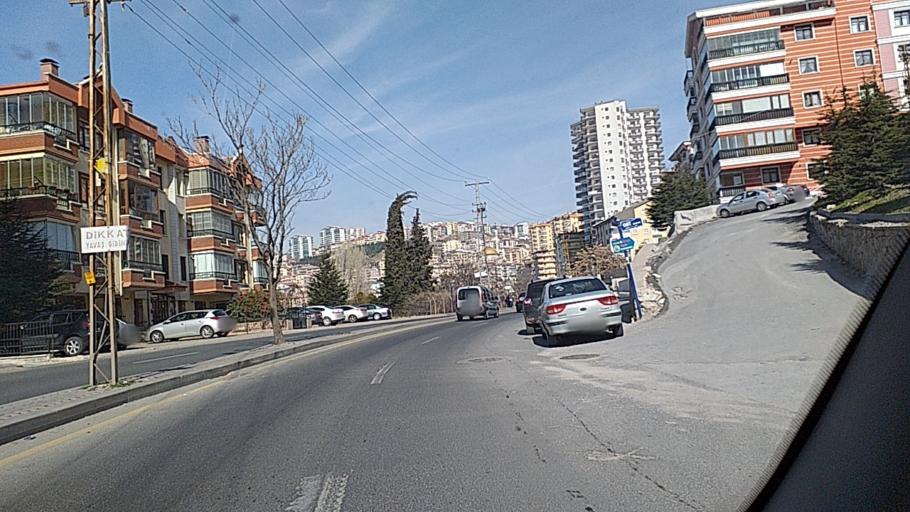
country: TR
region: Ankara
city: Ankara
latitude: 39.9847
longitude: 32.8239
